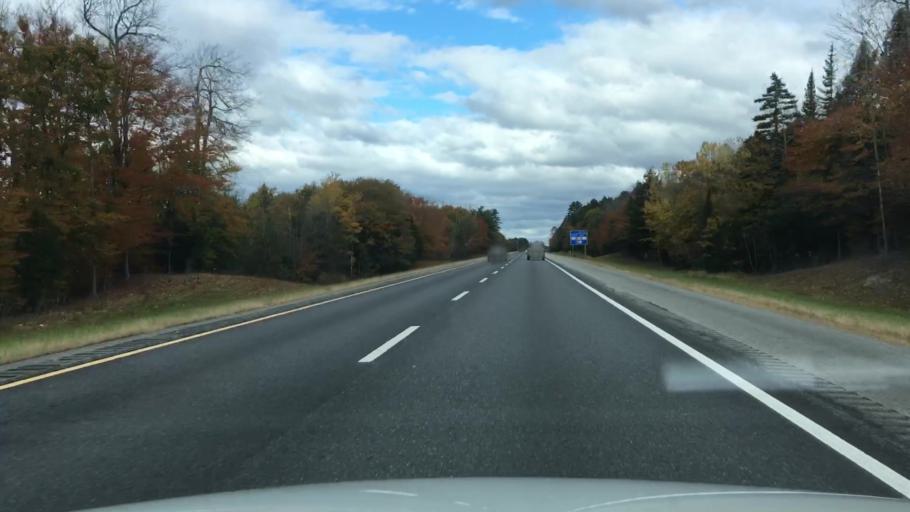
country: US
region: Maine
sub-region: Sagadahoc County
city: Richmond
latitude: 44.0838
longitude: -69.8761
